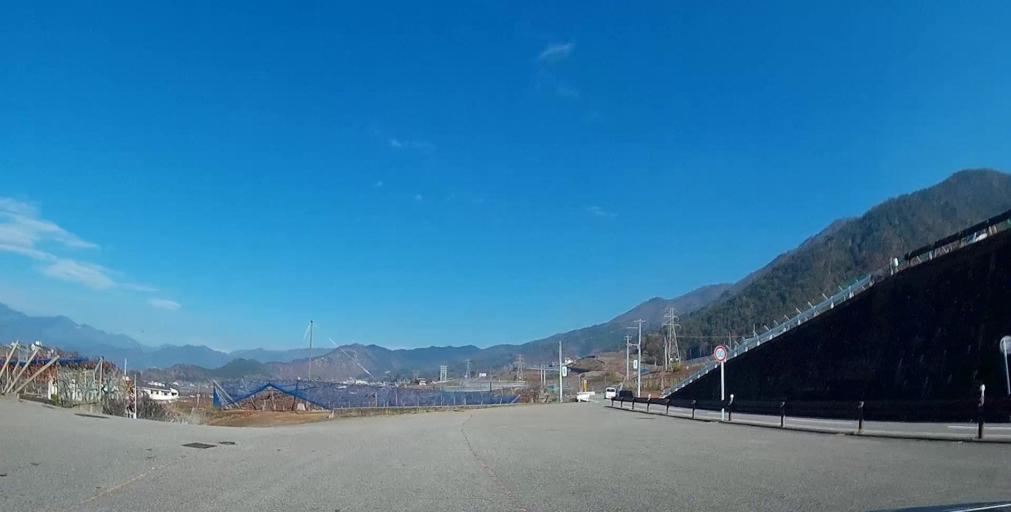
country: JP
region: Yamanashi
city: Enzan
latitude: 35.6641
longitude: 138.7387
